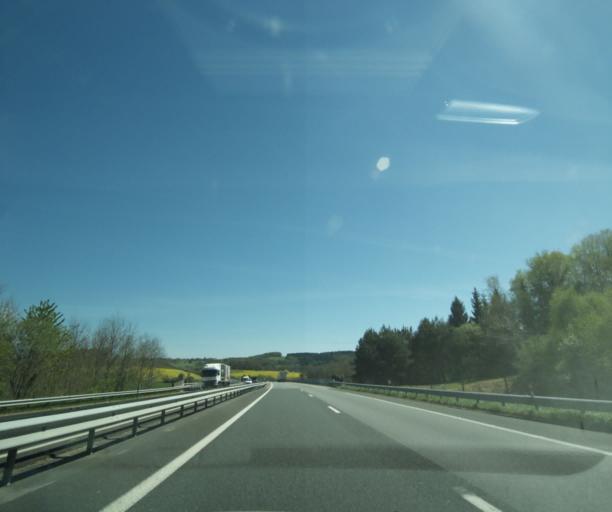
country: FR
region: Limousin
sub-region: Departement de la Correze
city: Vigeois
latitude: 45.4128
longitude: 1.5244
